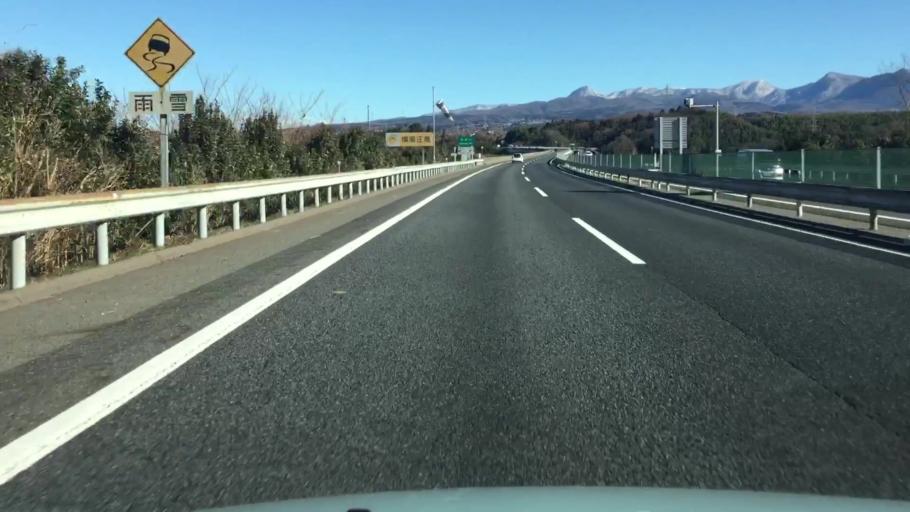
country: JP
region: Gunma
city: Shibukawa
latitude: 36.4799
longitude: 139.0200
